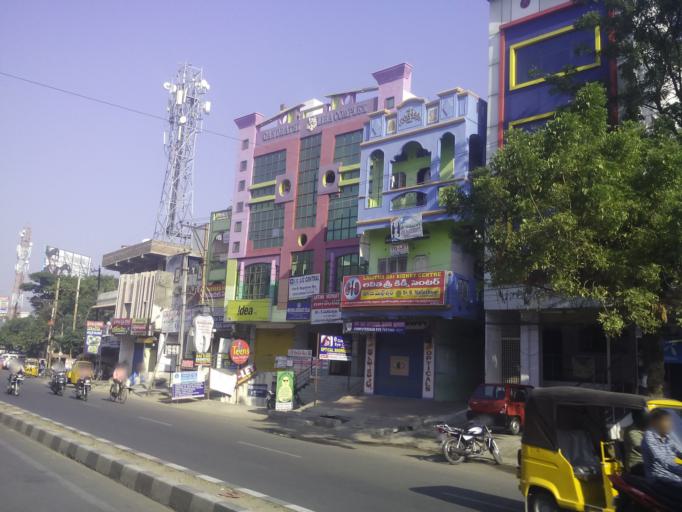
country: IN
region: Telangana
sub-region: Warangal
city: Warangal
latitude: 17.9900
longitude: 79.5956
